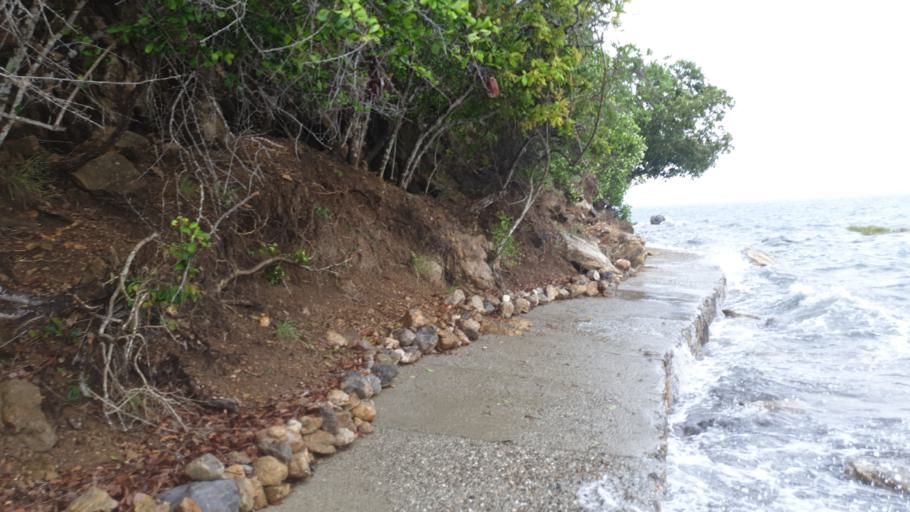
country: PG
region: National Capital
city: Port Moresby
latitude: -9.5364
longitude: 147.2899
